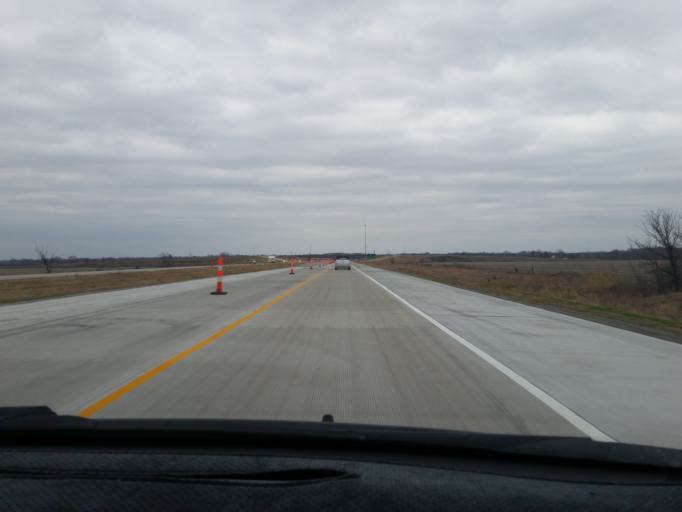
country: US
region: Kansas
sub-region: Douglas County
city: Eudora
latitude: 38.9352
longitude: -95.1593
